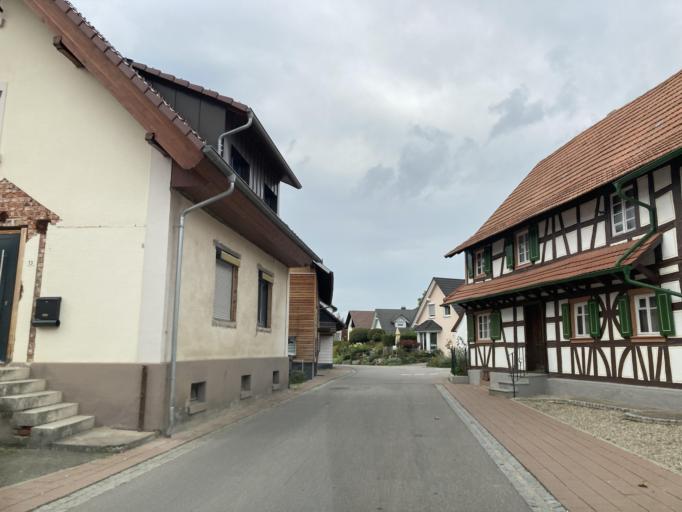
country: DE
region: Baden-Wuerttemberg
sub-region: Freiburg Region
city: Haslach
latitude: 48.5803
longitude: 8.0473
